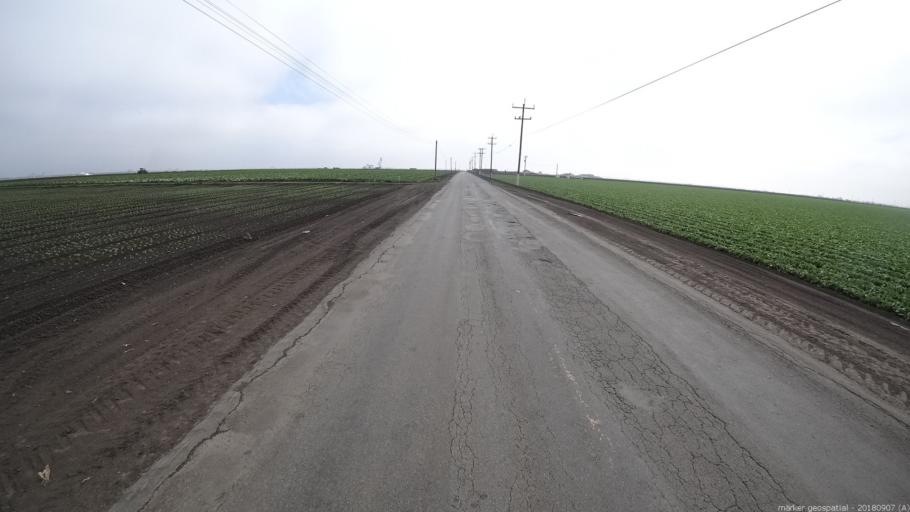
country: US
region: California
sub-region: Monterey County
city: Boronda
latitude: 36.6933
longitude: -121.7190
